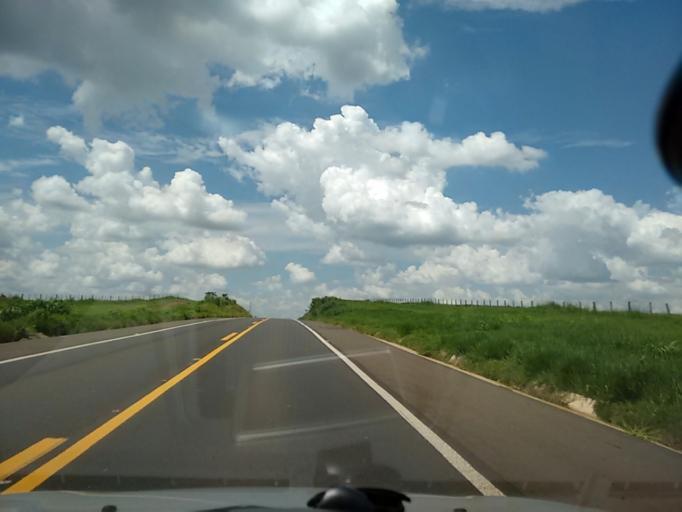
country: BR
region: Sao Paulo
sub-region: Osvaldo Cruz
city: Osvaldo Cruz
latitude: -21.8728
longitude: -50.8569
